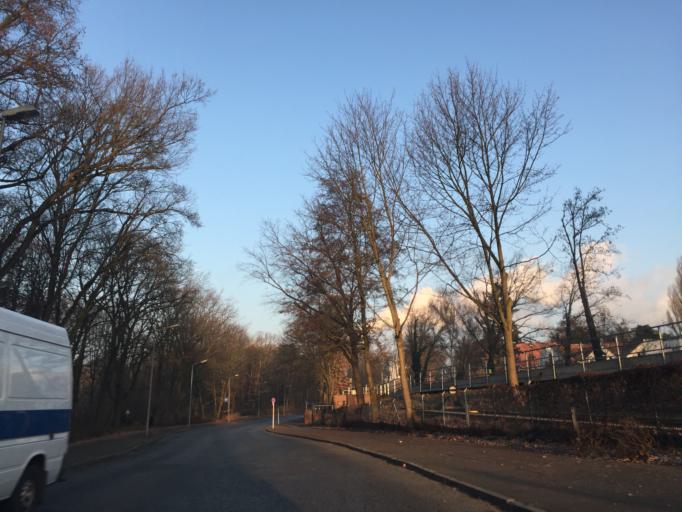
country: DE
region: Berlin
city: Haselhorst
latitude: 52.5218
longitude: 13.2460
